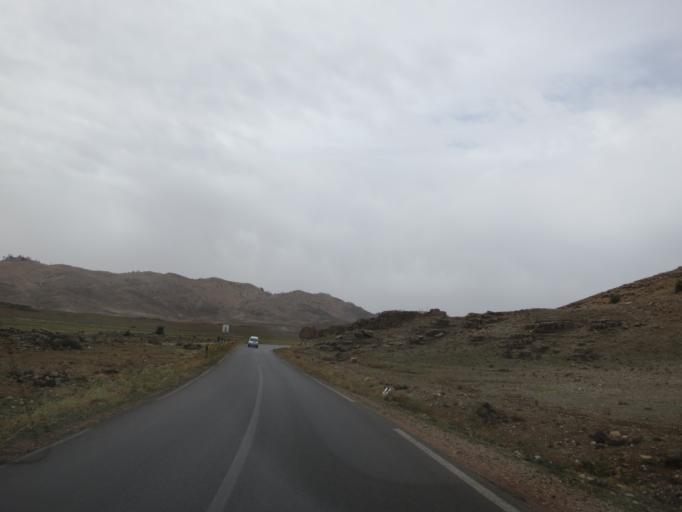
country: MA
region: Meknes-Tafilalet
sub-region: Khenifra
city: Itzer
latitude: 33.0780
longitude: -5.0194
